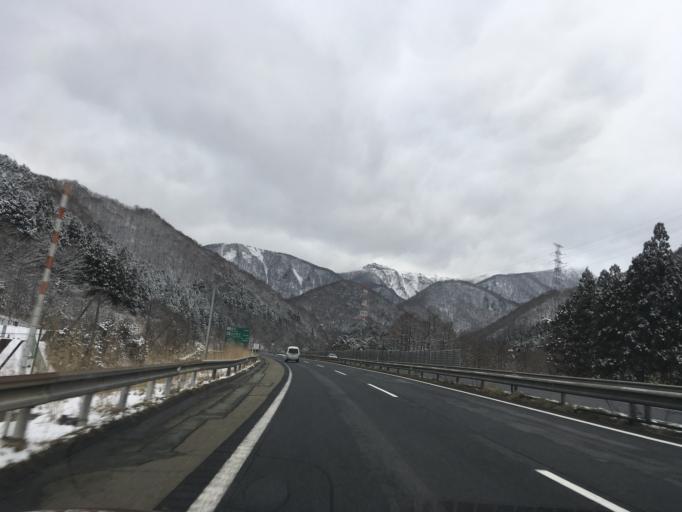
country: JP
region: Yamagata
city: Yamagata-shi
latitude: 38.2264
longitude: 140.5002
